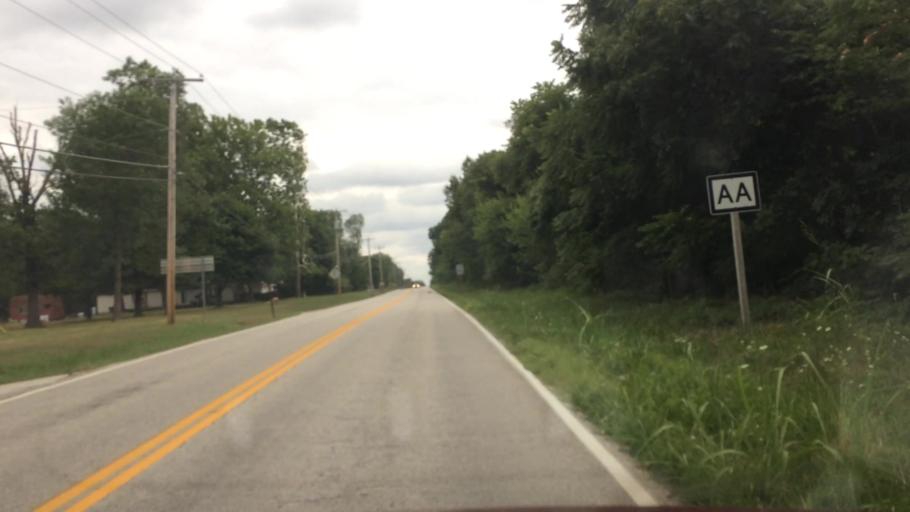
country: US
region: Missouri
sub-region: Greene County
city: Springfield
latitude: 37.2953
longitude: -93.2630
